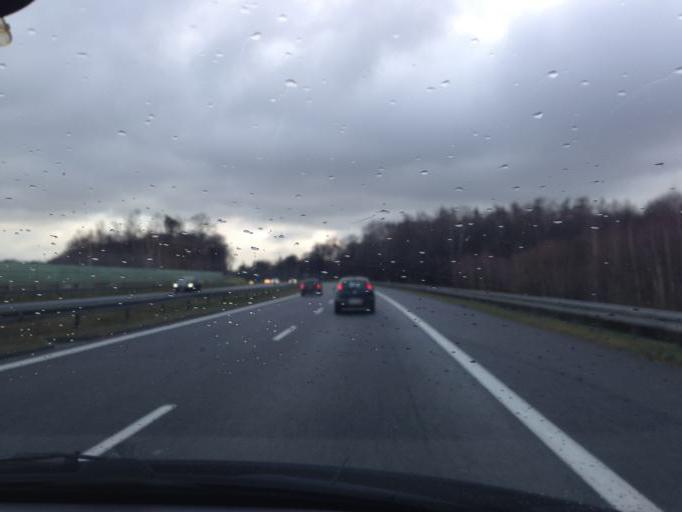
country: PL
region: Opole Voivodeship
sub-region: Powiat strzelecki
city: Ujazd
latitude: 50.4343
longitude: 18.3681
